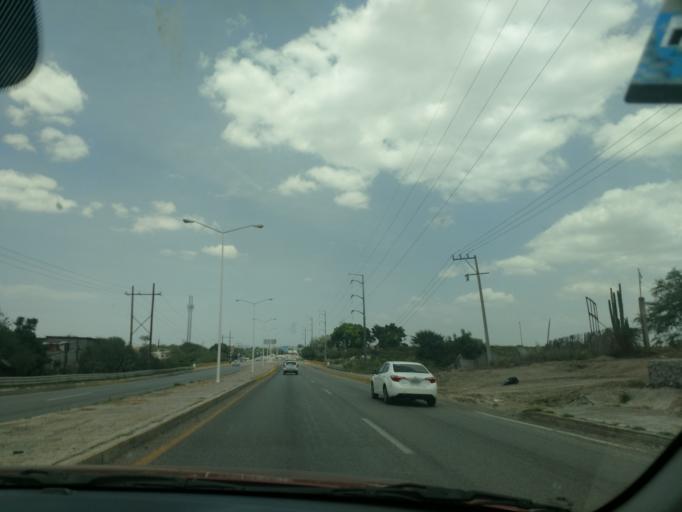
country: MX
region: San Luis Potosi
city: Rio Verde
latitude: 21.9218
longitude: -99.9670
